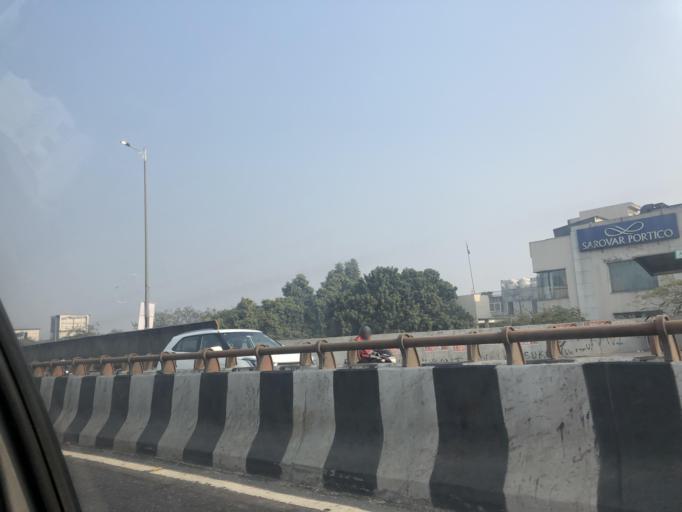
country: IN
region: NCT
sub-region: Central Delhi
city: Karol Bagh
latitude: 28.6257
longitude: 77.1345
